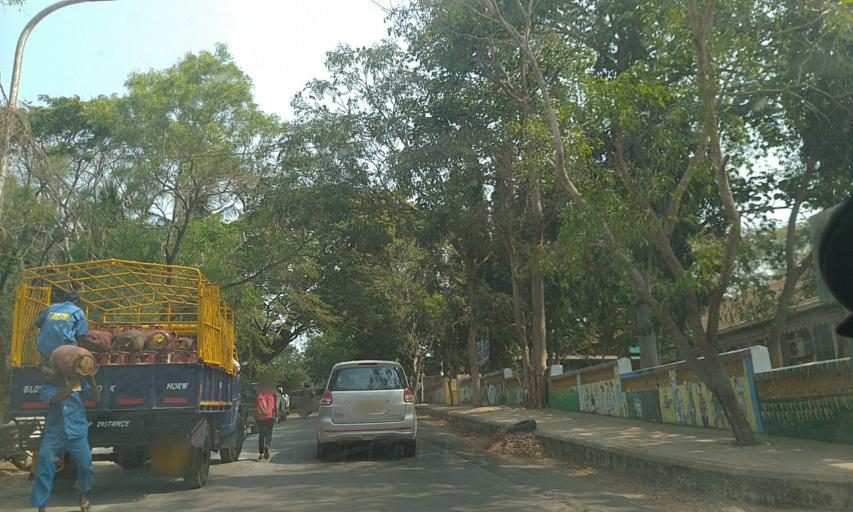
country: IN
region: Goa
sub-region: North Goa
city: Panaji
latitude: 15.4885
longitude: 73.8271
